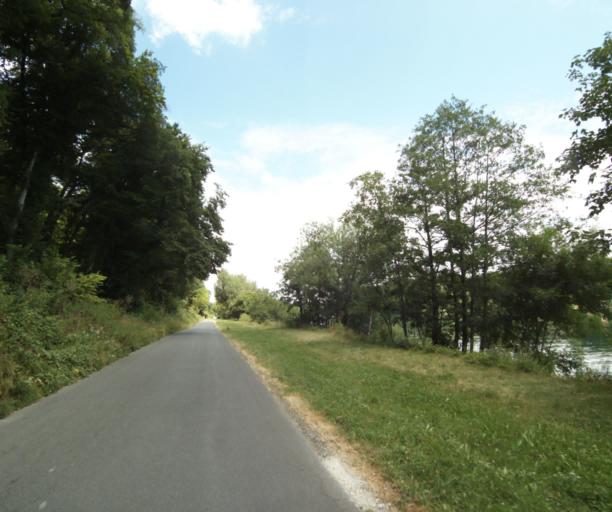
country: FR
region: Ile-de-France
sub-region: Departement de Seine-et-Marne
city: Samois-sur-Seine
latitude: 48.4425
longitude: 2.7482
